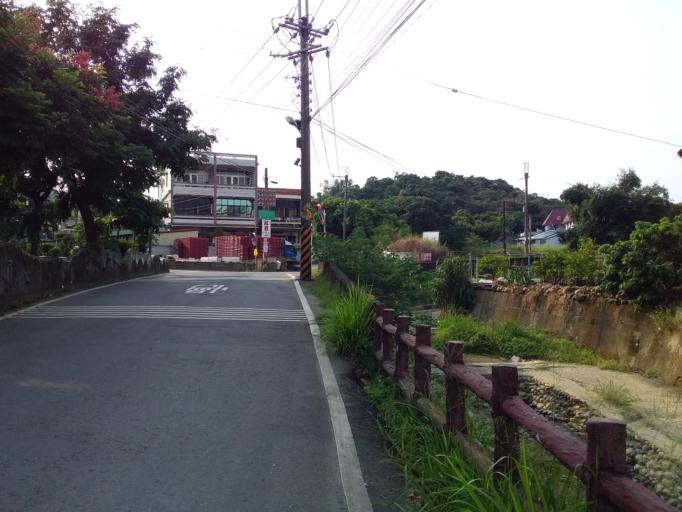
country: TW
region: Taiwan
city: Fengshan
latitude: 22.6890
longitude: 120.4092
